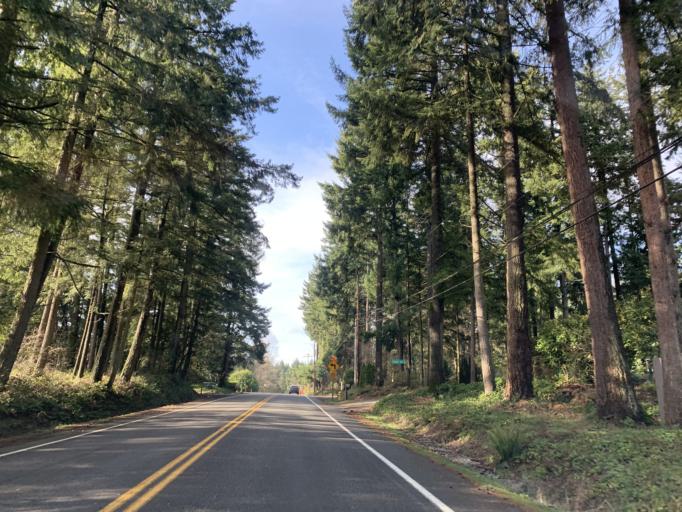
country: US
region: Washington
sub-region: King County
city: Lakeland South
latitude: 47.2885
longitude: -122.2954
